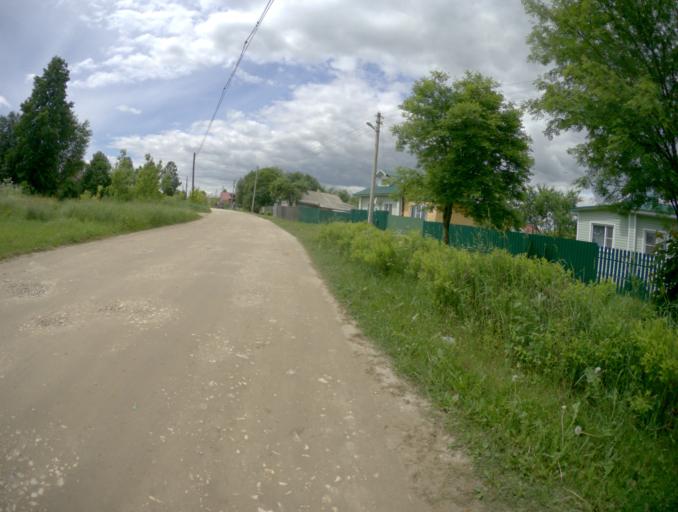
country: RU
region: Ivanovo
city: Savino
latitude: 56.5898
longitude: 41.2219
